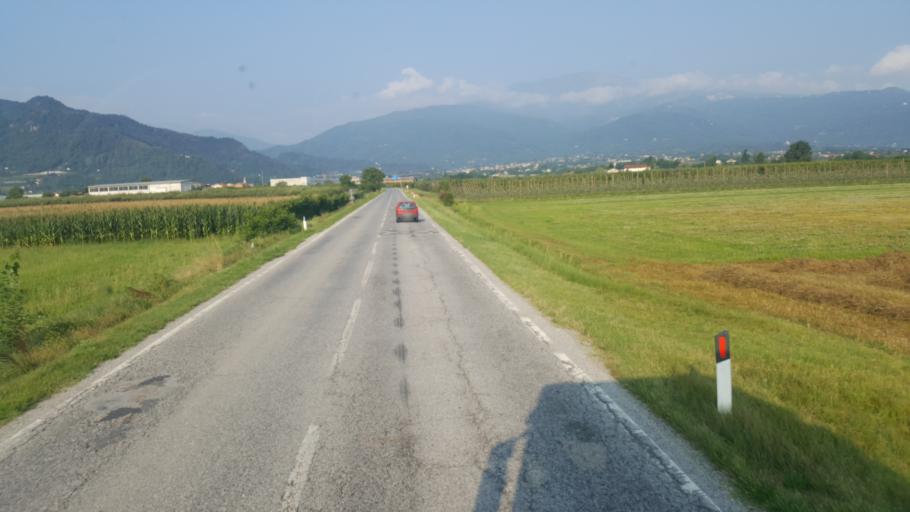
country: IT
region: Piedmont
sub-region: Provincia di Cuneo
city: Barge
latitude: 44.7395
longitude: 7.3691
